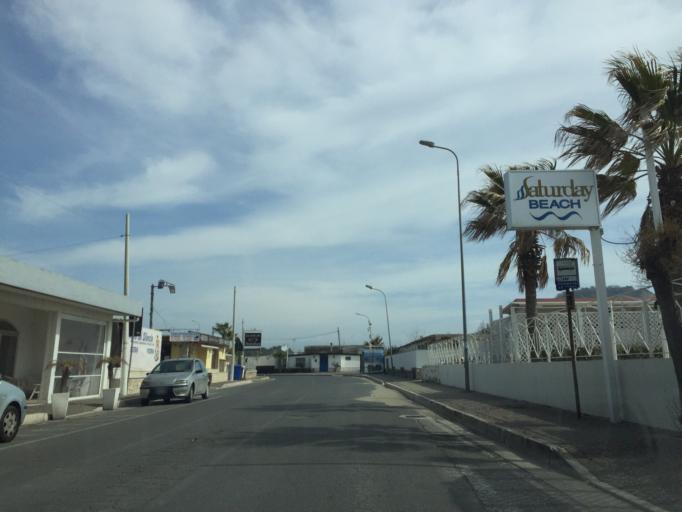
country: IT
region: Campania
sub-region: Provincia di Napoli
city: Bacoli
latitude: 40.7885
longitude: 14.0738
